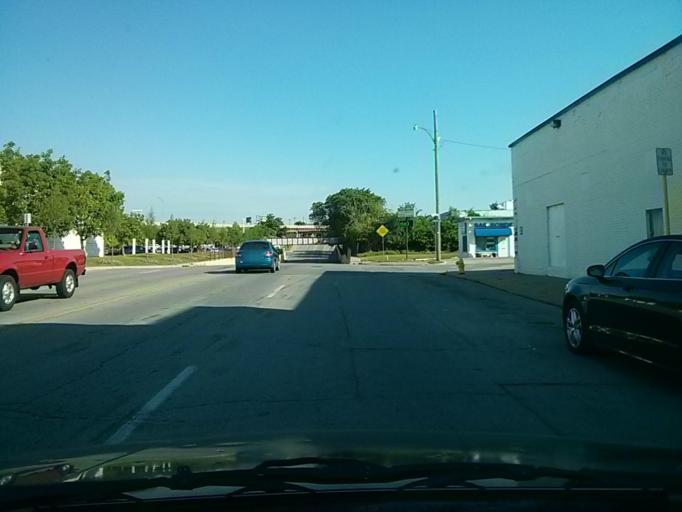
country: US
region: Oklahoma
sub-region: Tulsa County
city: Tulsa
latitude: 36.1577
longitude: -95.9975
